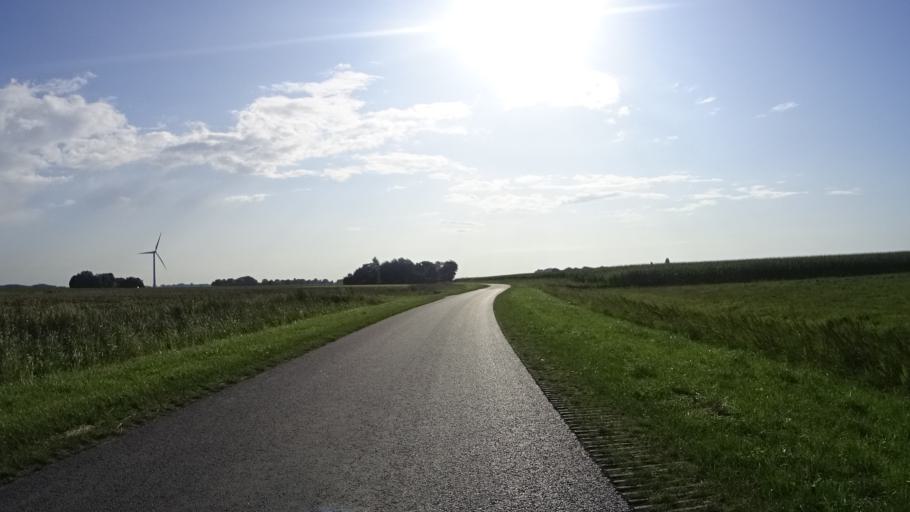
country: NL
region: Friesland
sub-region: Gemeente Harlingen
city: Harlingen
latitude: 53.1198
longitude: 5.4252
